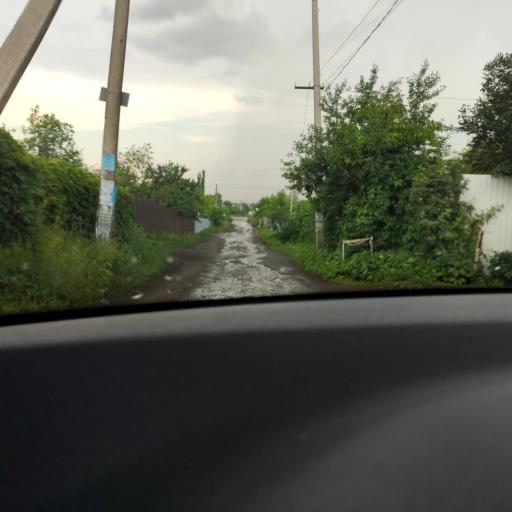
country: RU
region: Samara
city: Novosemeykino
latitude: 53.4028
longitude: 50.3154
